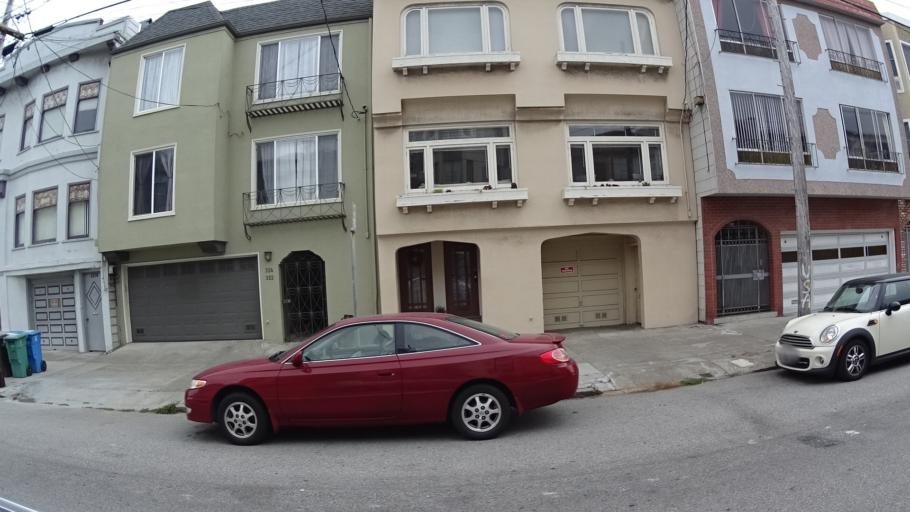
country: US
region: California
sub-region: San Francisco County
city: San Francisco
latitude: 37.7834
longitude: -122.4839
